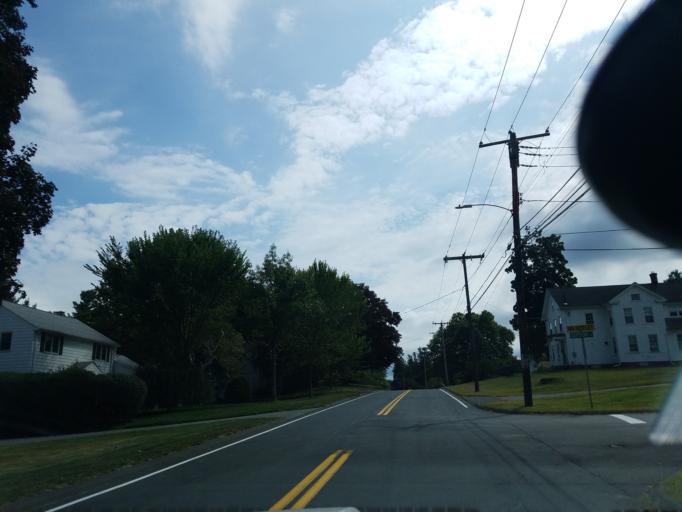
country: US
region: Connecticut
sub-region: Hartford County
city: Wethersfield
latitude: 41.6800
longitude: -72.6470
